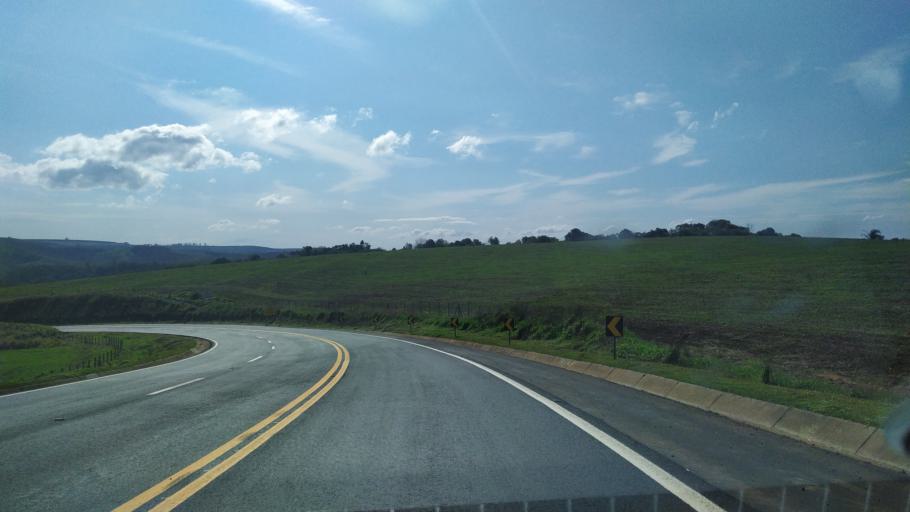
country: BR
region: Parana
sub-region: Telemaco Borba
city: Telemaco Borba
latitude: -24.2787
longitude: -50.7135
